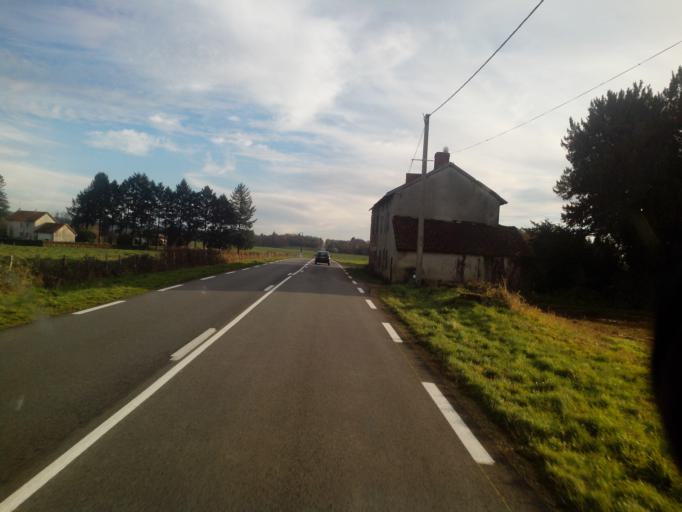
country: FR
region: Limousin
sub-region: Departement de la Haute-Vienne
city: Neuvic-Entier
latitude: 45.7528
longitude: 1.5953
